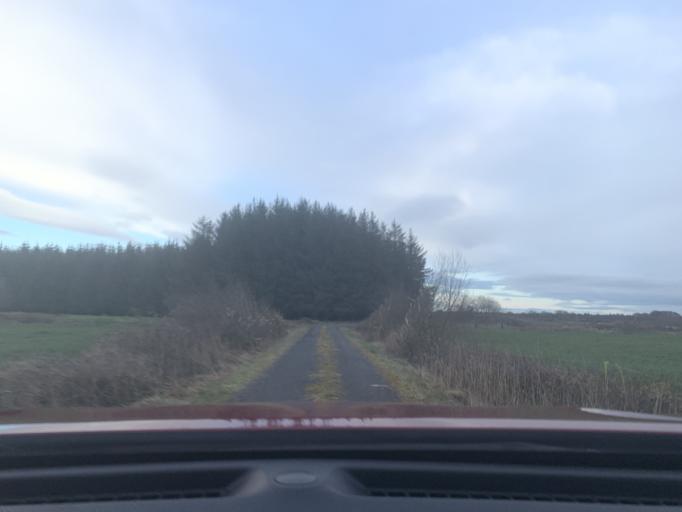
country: IE
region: Connaught
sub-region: Roscommon
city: Ballaghaderreen
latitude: 53.8899
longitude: -8.5825
